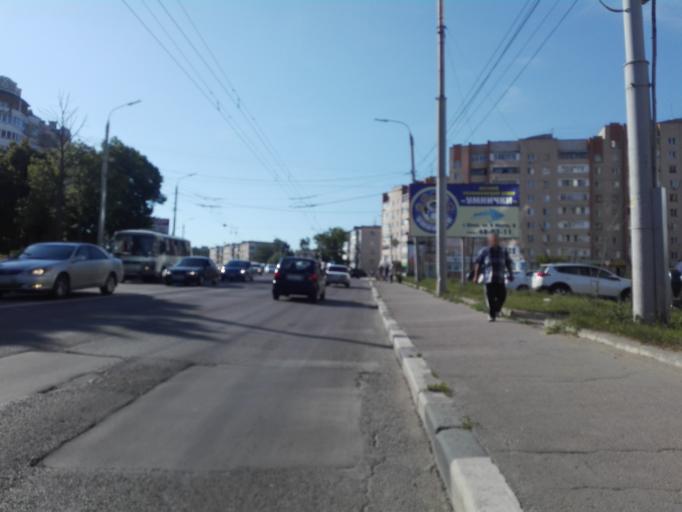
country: RU
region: Orjol
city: Orel
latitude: 52.9782
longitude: 36.0785
